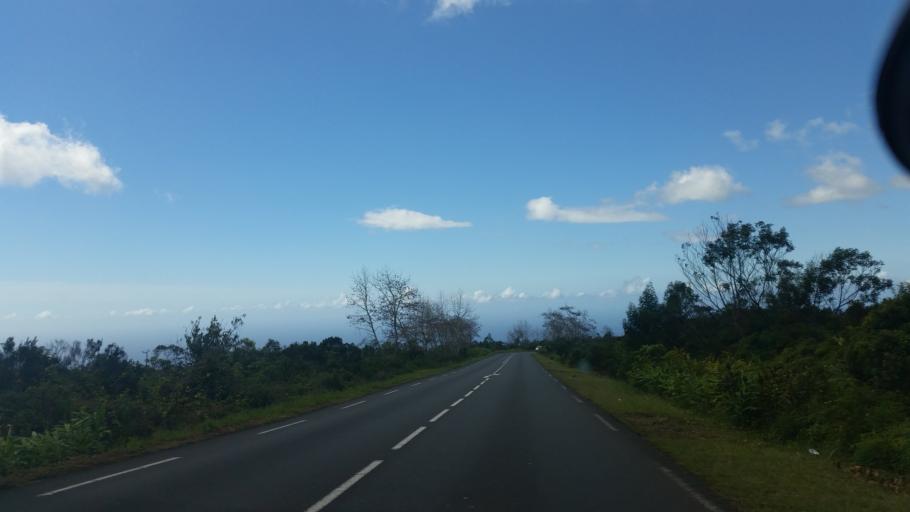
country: RE
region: Reunion
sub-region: Reunion
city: Saint-Benoit
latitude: -21.1148
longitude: 55.6519
